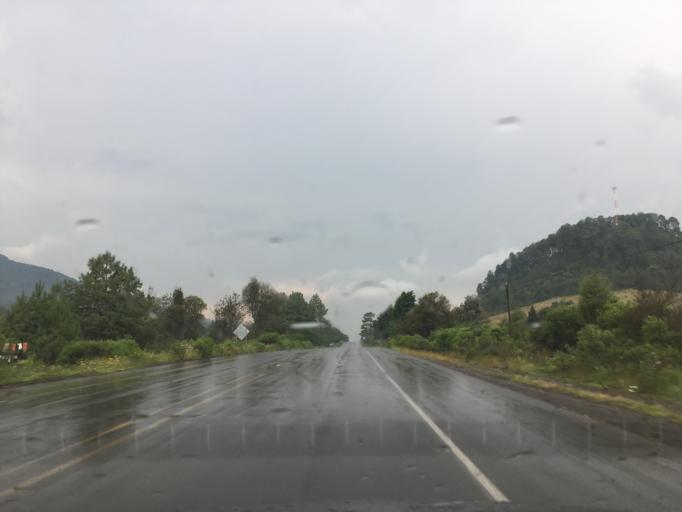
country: MX
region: Michoacan
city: Angahuan
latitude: 19.5607
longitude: -102.2280
